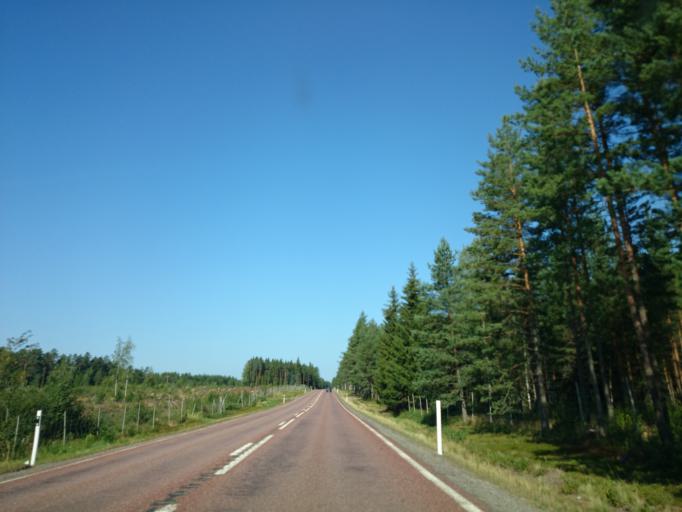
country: SE
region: Gaevleborg
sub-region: Hudiksvalls Kommun
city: Delsbo
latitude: 61.7885
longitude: 16.6038
